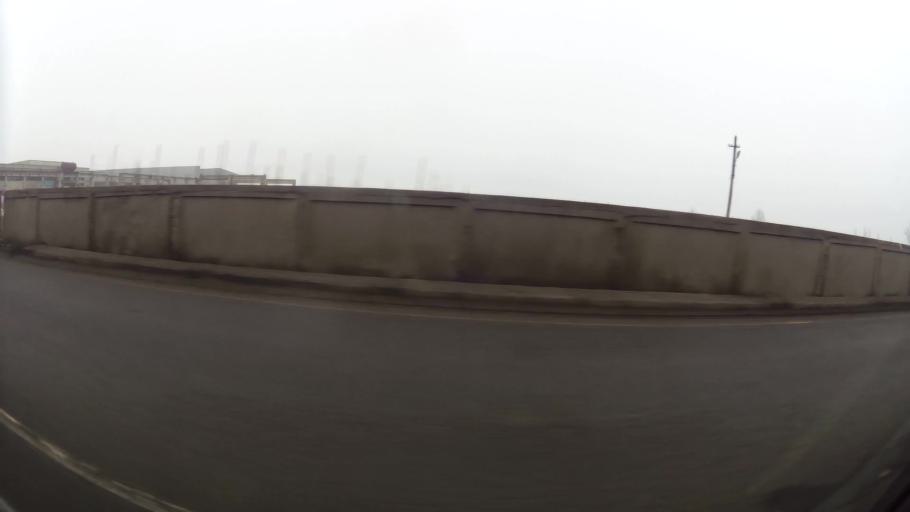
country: RO
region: Ilfov
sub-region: Comuna Bragadiru
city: Bragadiru
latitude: 44.3874
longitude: 25.9878
